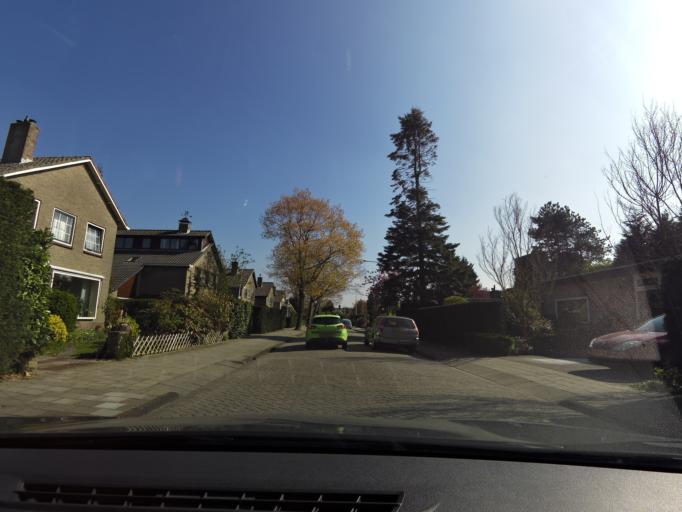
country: NL
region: South Holland
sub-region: Gemeente Maassluis
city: Maassluis
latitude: 51.9333
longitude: 4.2670
